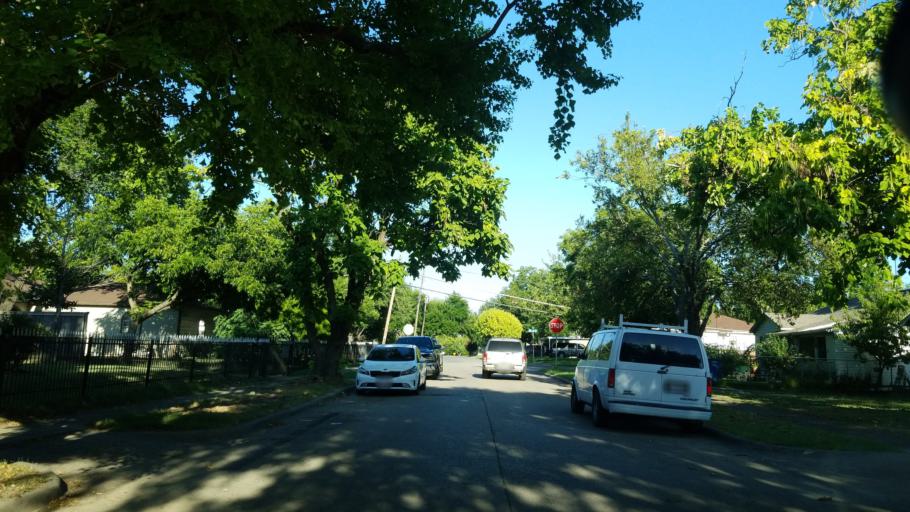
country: US
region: Texas
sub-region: Dallas County
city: Dallas
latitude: 32.7769
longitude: -96.7097
